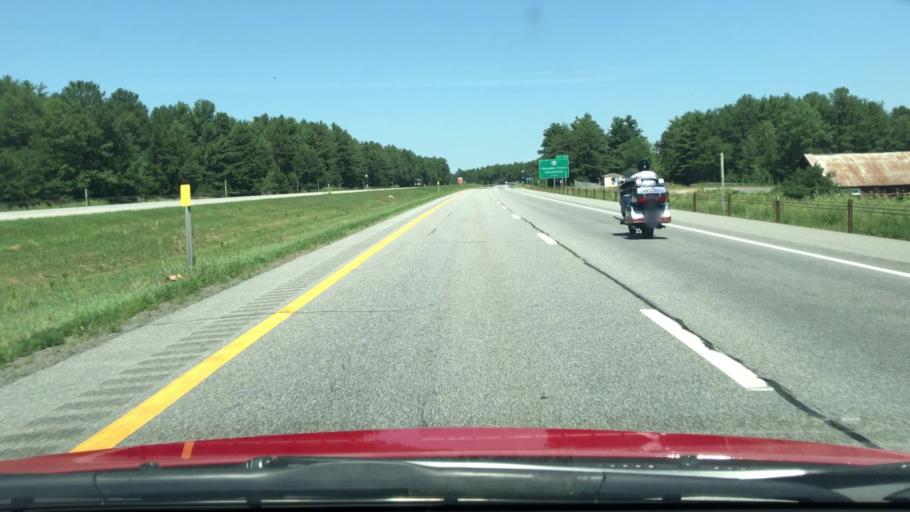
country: US
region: New York
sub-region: Essex County
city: Keeseville
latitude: 44.4792
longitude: -73.4887
